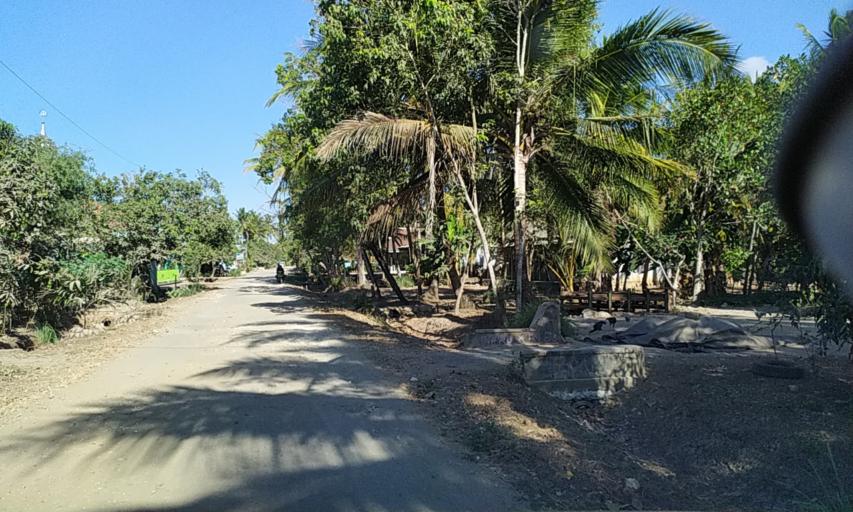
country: ID
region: Central Java
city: Kalenaren
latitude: -7.5811
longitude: 108.8004
